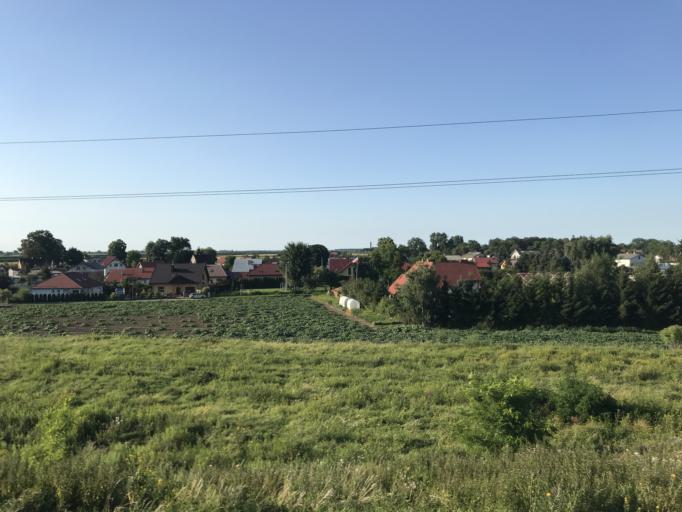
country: PL
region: Pomeranian Voivodeship
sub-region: Powiat malborski
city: Lisewo Malborskie
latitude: 54.0929
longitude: 18.8279
